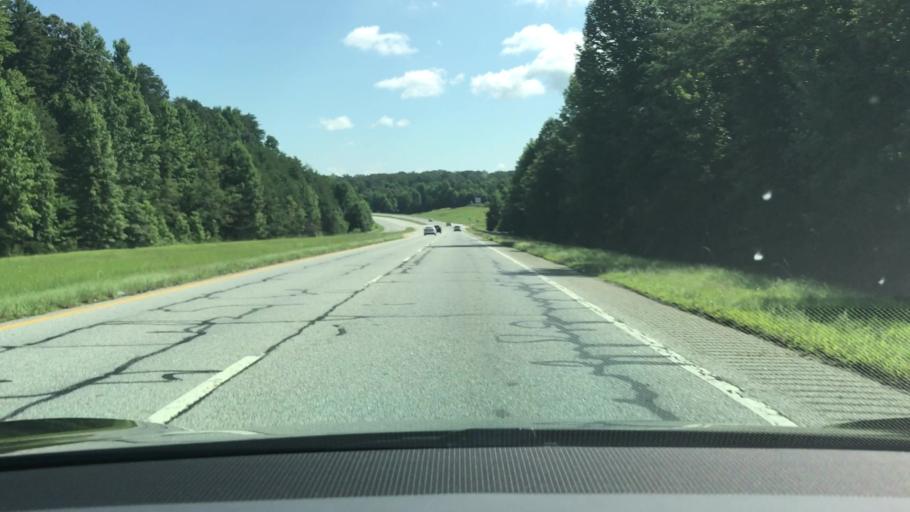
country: US
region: Georgia
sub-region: Habersham County
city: Clarkesville
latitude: 34.6568
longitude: -83.4388
